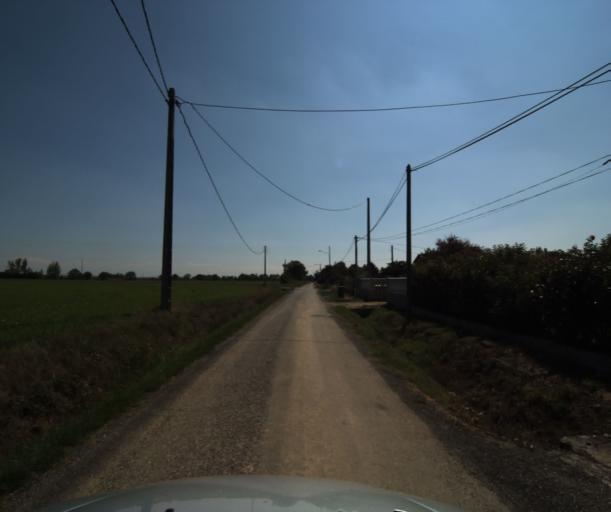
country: FR
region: Midi-Pyrenees
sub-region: Departement de la Haute-Garonne
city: Labastidette
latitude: 43.4406
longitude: 1.2635
